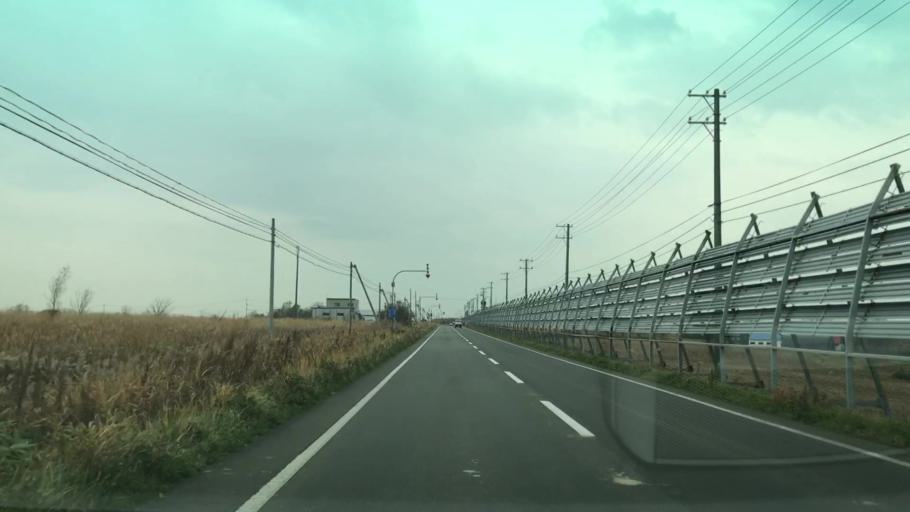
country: JP
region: Hokkaido
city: Ishikari
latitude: 43.2853
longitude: 141.4098
